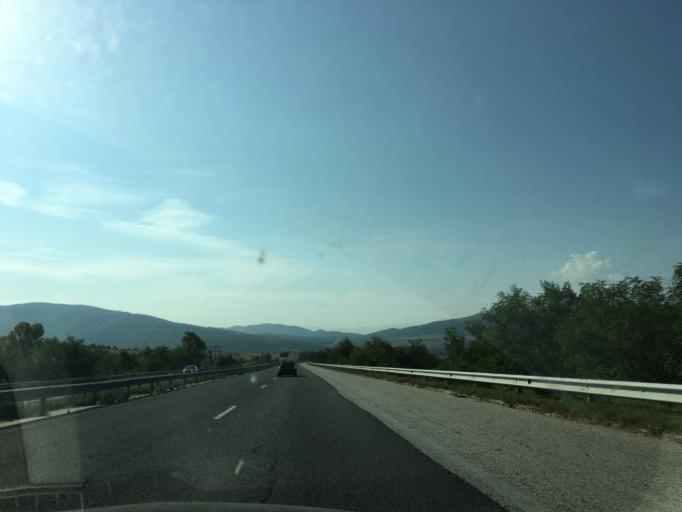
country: BG
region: Sofiya
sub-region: Obshtina Ikhtiman
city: Ikhtiman
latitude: 42.4239
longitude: 23.8558
